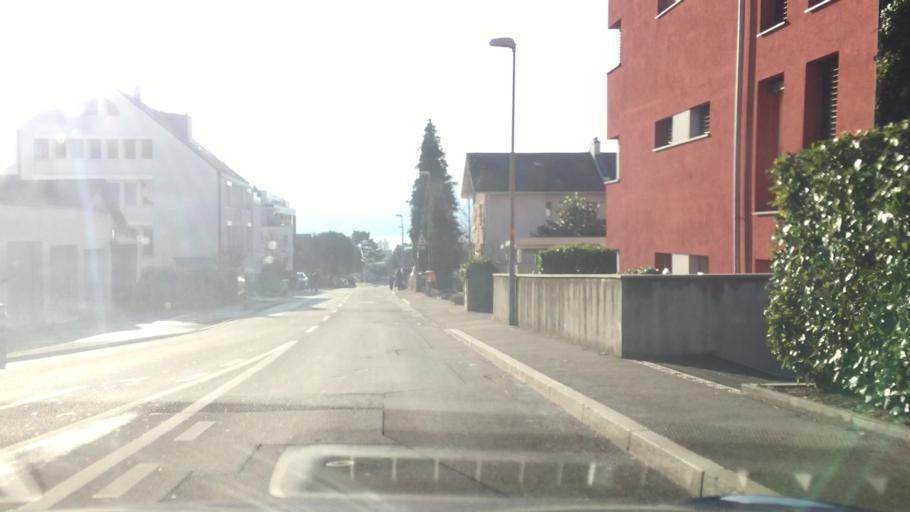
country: CH
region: Vaud
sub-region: Lavaux-Oron District
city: Paudex
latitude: 46.5084
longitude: 6.6697
